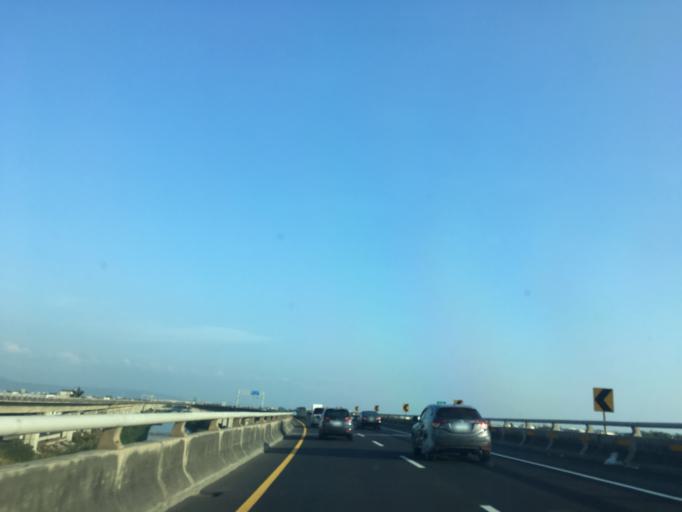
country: TW
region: Taiwan
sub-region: Changhua
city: Chang-hua
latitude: 24.0006
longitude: 120.4954
